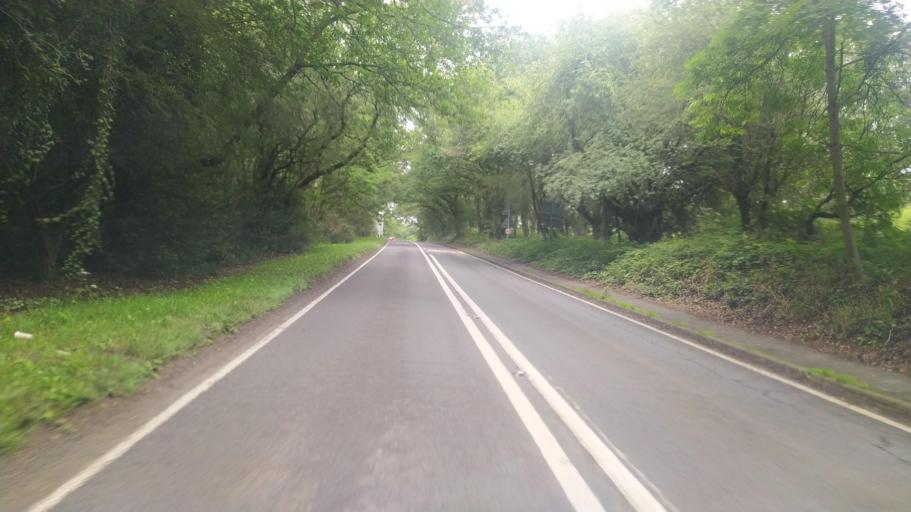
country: GB
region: England
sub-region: Hampshire
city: Liphook
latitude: 51.0659
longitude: -0.8087
